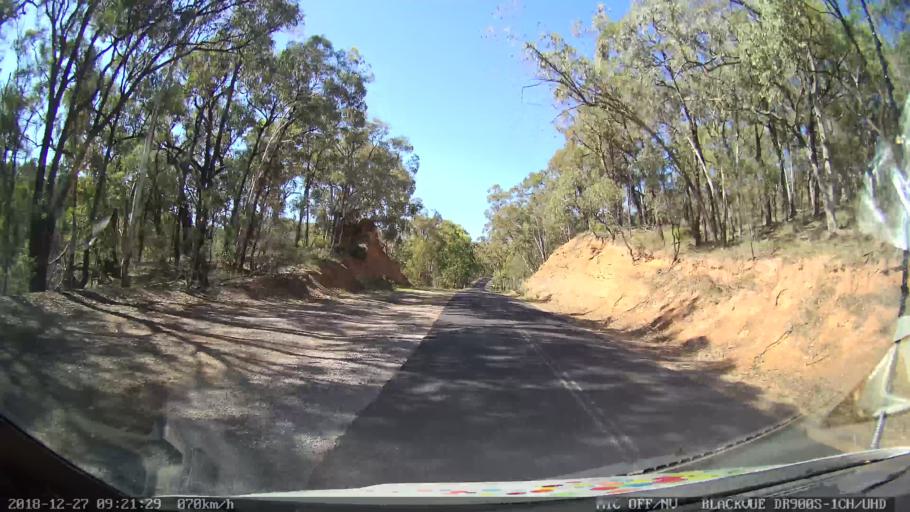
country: AU
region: New South Wales
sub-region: Lithgow
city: Portland
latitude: -33.1242
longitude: 150.0161
